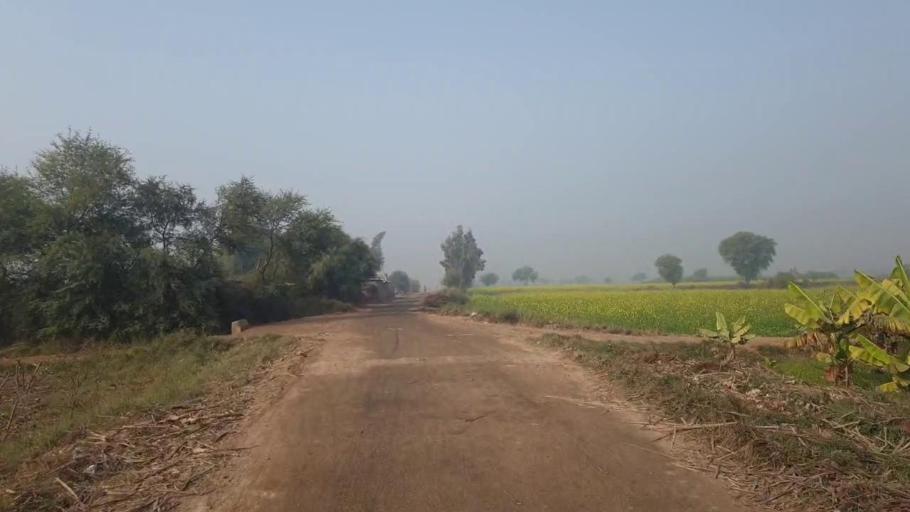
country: PK
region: Sindh
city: Tando Adam
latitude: 25.7956
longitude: 68.6176
